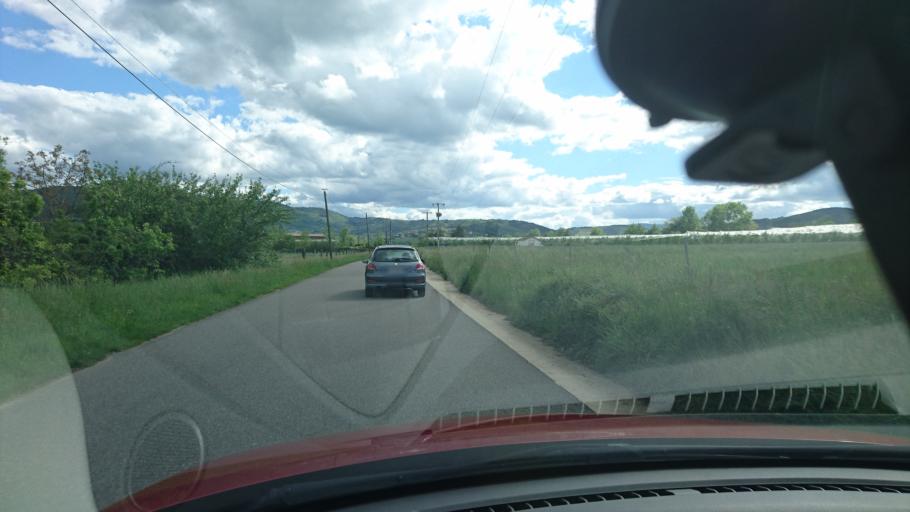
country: FR
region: Rhone-Alpes
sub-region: Departement de la Loire
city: Maclas
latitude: 45.3568
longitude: 4.6837
